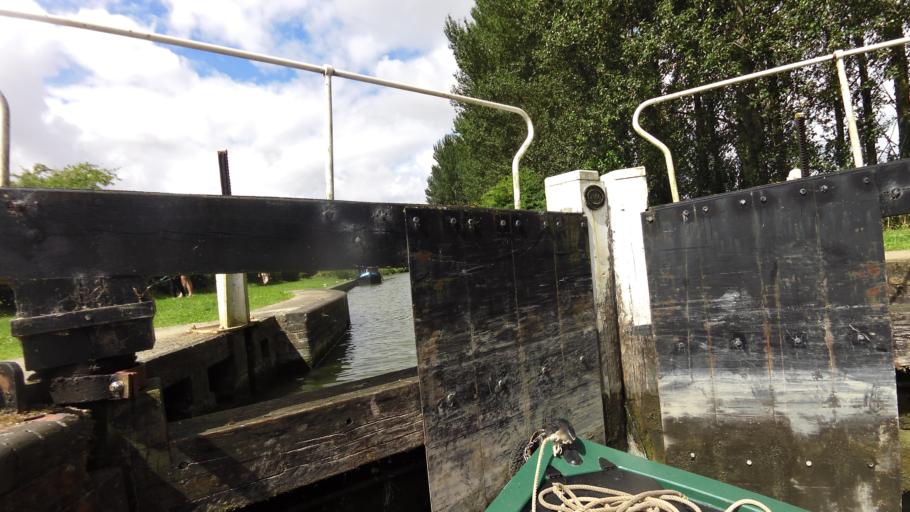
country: GB
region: England
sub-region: Wiltshire
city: Burbage
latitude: 51.3588
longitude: -1.6404
